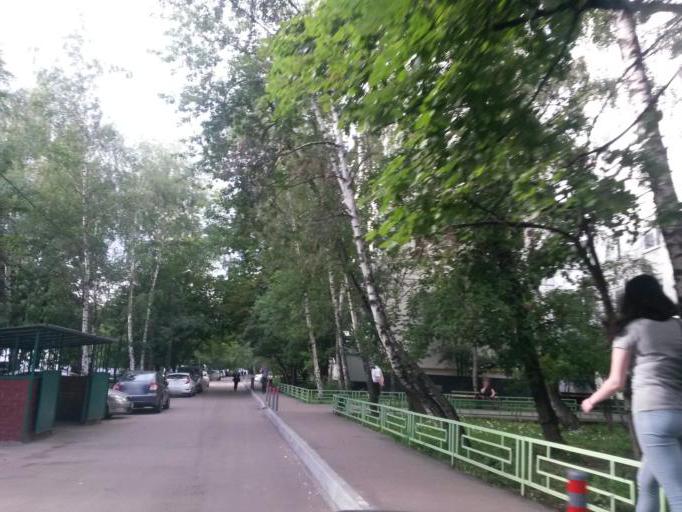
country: RU
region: Moscow
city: Orekhovo-Borisovo
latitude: 55.6073
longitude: 37.7168
